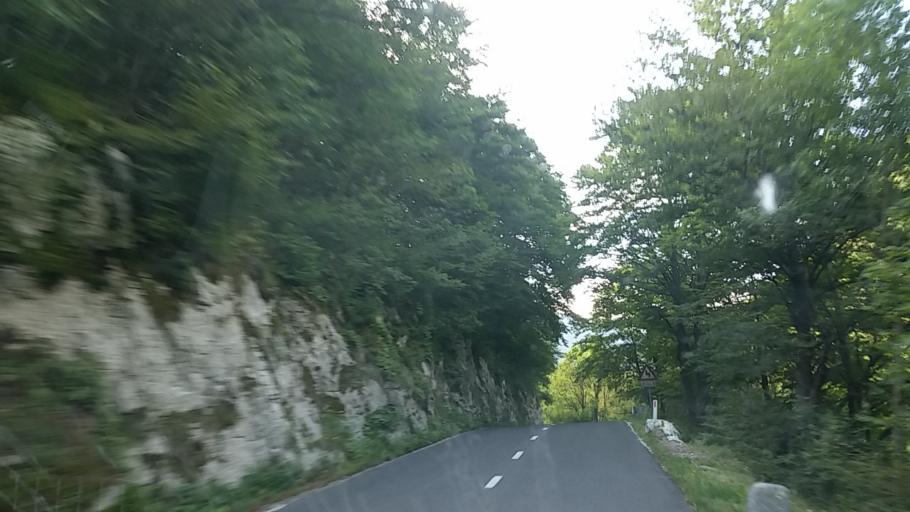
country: SI
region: Bovec
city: Bovec
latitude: 46.3673
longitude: 13.5882
